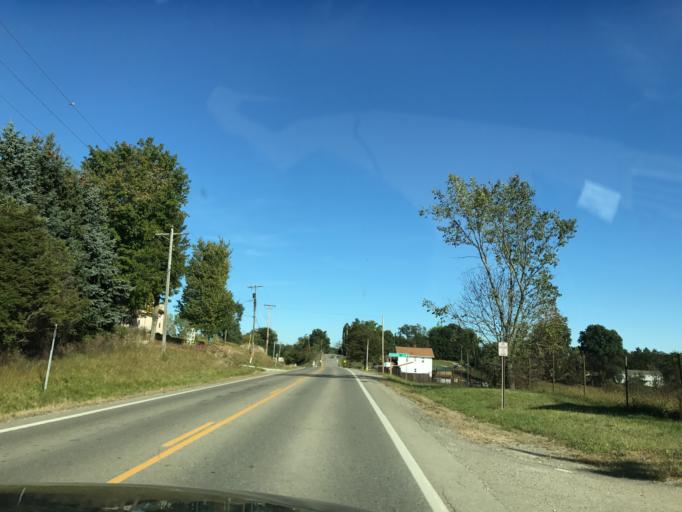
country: US
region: Ohio
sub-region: Belmont County
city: Bethesda
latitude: 40.0710
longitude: -81.0078
